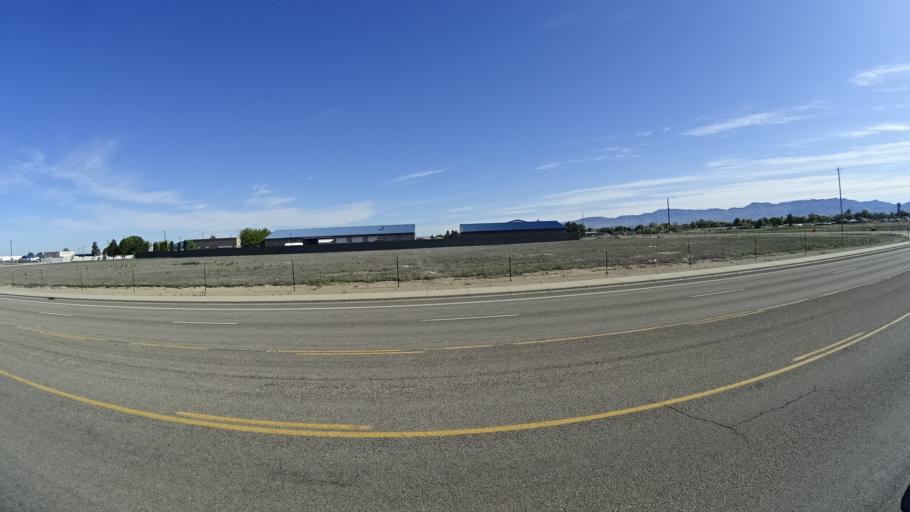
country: US
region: Idaho
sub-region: Ada County
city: Garden City
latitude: 43.5753
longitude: -116.2596
